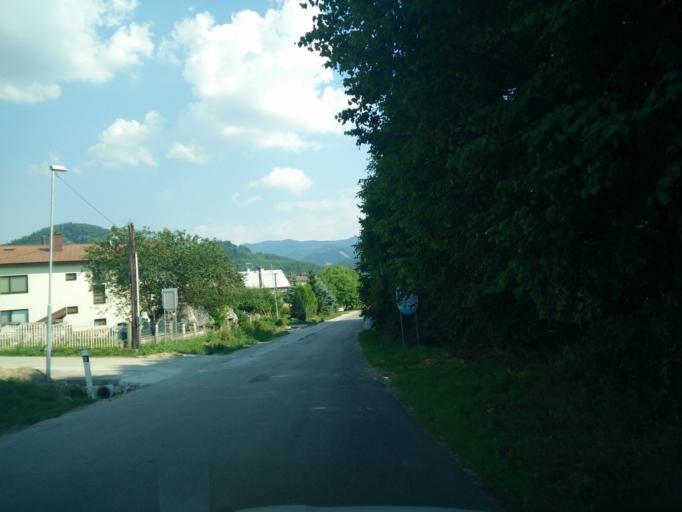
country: SK
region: Zilinsky
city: Rajec
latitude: 49.1028
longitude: 18.7025
